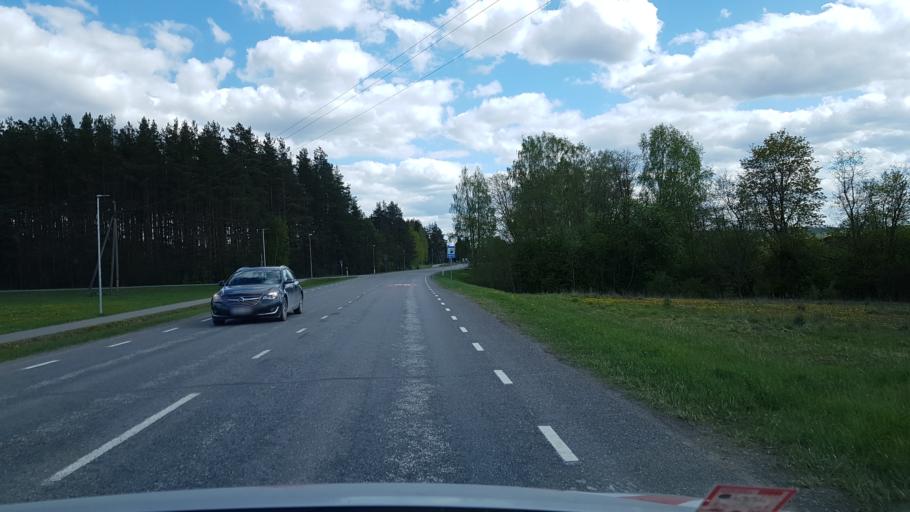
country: EE
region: Tartu
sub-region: UElenurme vald
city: Ulenurme
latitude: 58.3036
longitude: 26.8615
